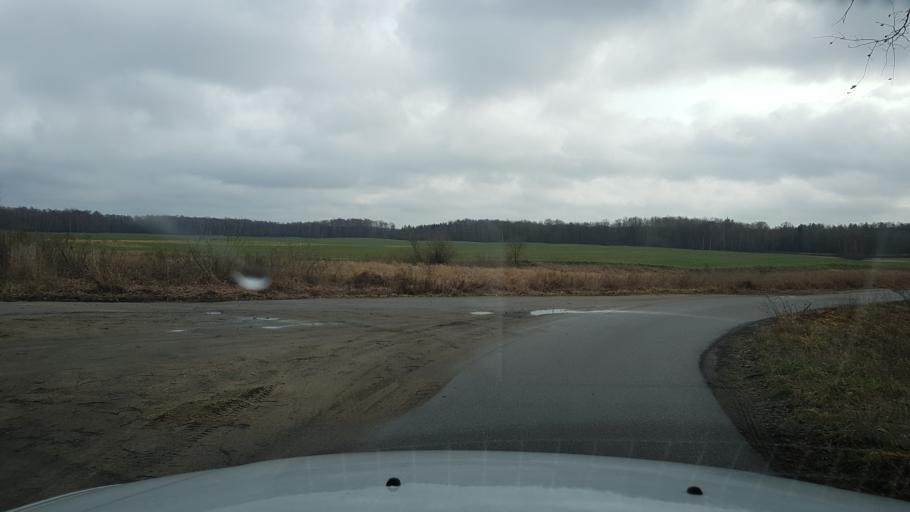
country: PL
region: West Pomeranian Voivodeship
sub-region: Powiat szczecinecki
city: Szczecinek
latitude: 53.7048
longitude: 16.7686
